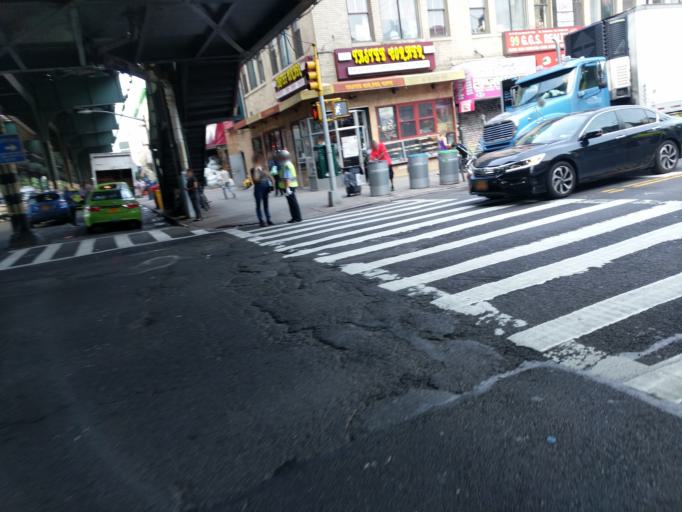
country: US
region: New York
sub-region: Queens County
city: Long Island City
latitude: 40.7670
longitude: -73.9214
